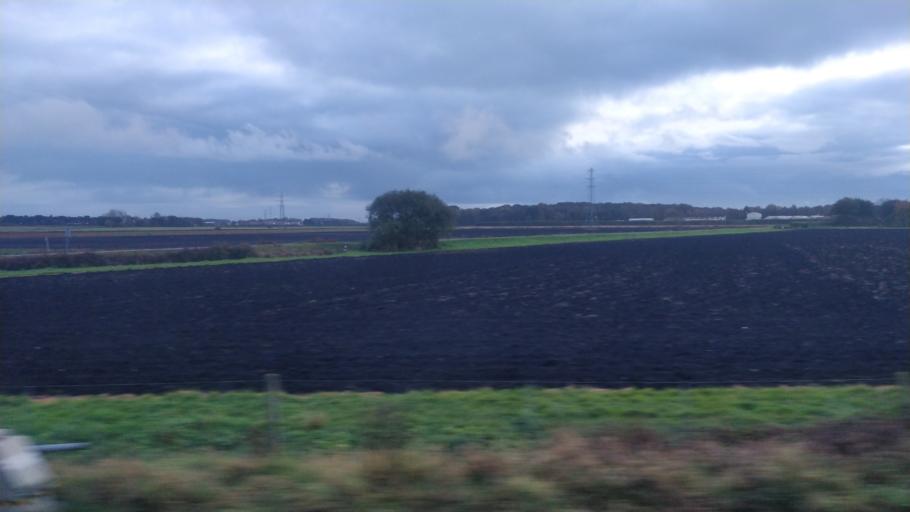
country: GB
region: England
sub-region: Sefton
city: Southport
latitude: 53.6334
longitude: -2.9509
